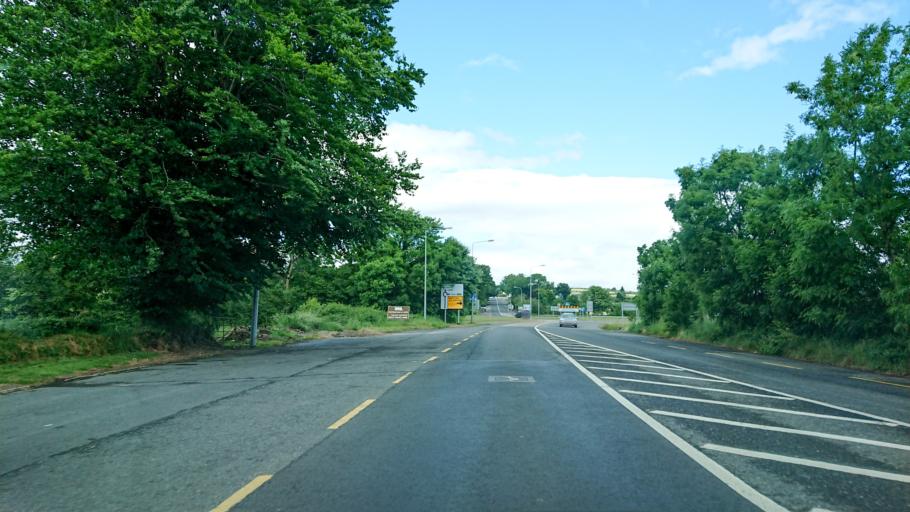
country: IE
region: Leinster
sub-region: Kilkenny
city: Mooncoin
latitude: 52.2357
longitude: -7.2461
